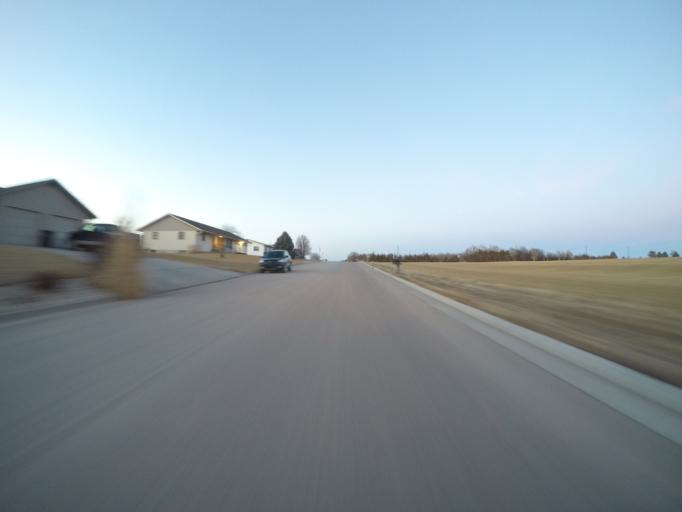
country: US
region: Kansas
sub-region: Clay County
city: Clay Center
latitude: 39.3925
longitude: -97.1187
